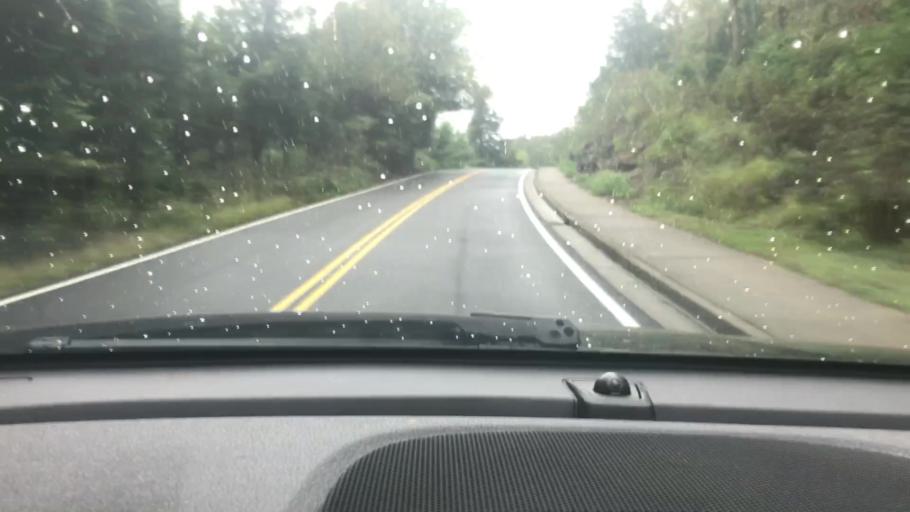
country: US
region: Tennessee
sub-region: Cheatham County
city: Kingston Springs
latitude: 36.0926
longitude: -87.1106
